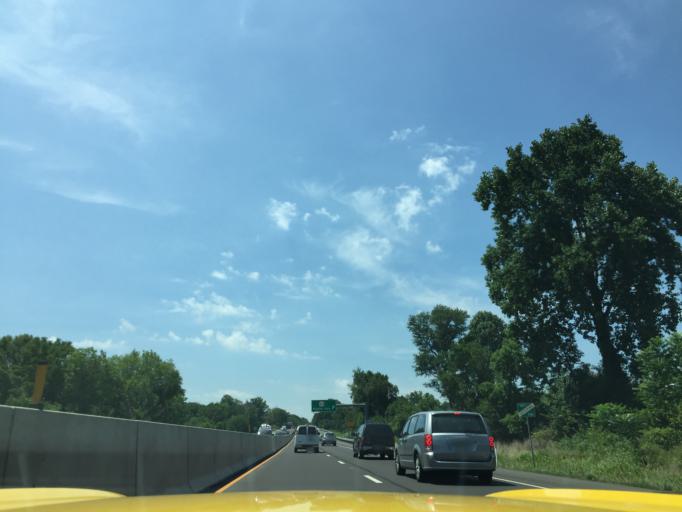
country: US
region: Pennsylvania
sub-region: Bucks County
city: Woodbourne
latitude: 40.1821
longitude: -74.9029
